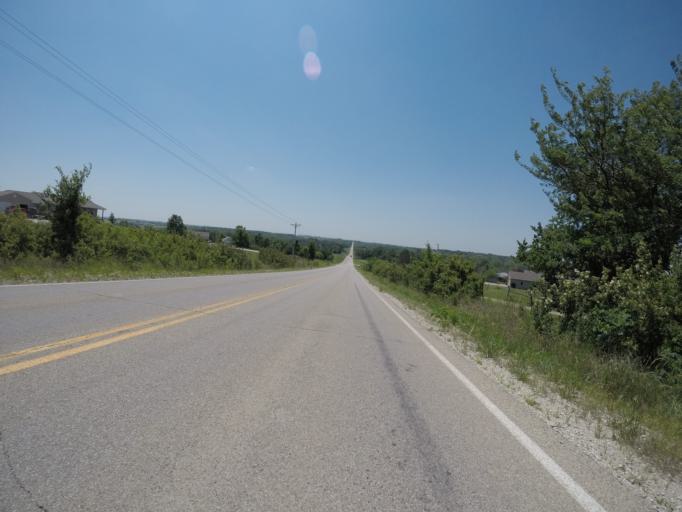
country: US
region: Kansas
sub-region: Pottawatomie County
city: Westmoreland
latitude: 39.2573
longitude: -96.4451
